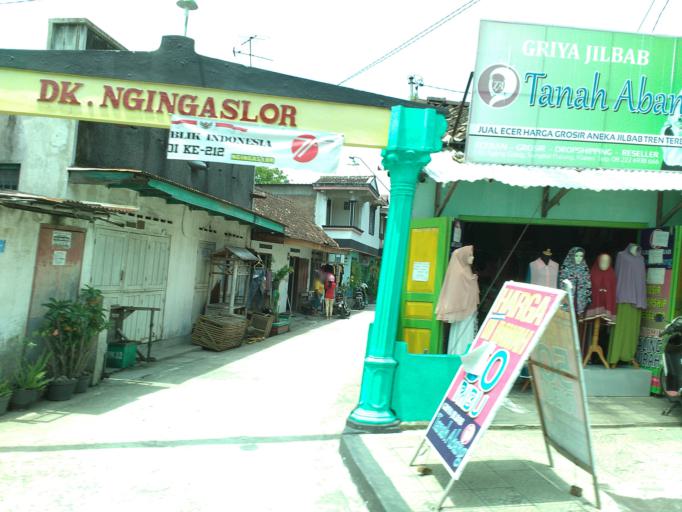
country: ID
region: Central Java
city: Klaten
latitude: -7.6912
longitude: 110.6123
